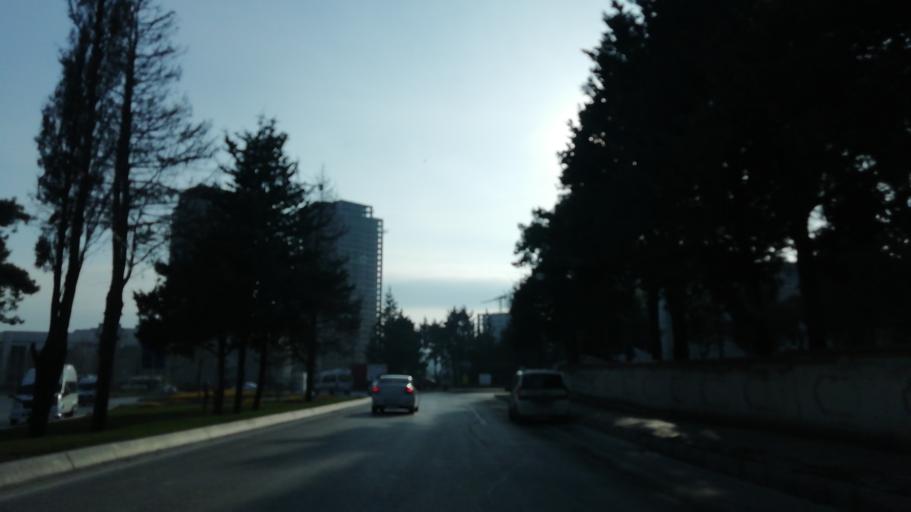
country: TR
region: Istanbul
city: Esenyurt
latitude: 41.0755
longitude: 28.6554
